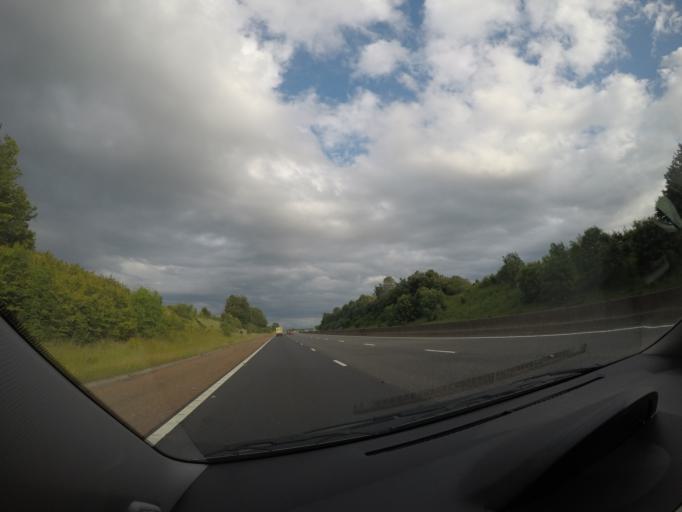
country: GB
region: England
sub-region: Cumbria
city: Penrith
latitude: 54.6805
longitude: -2.7848
